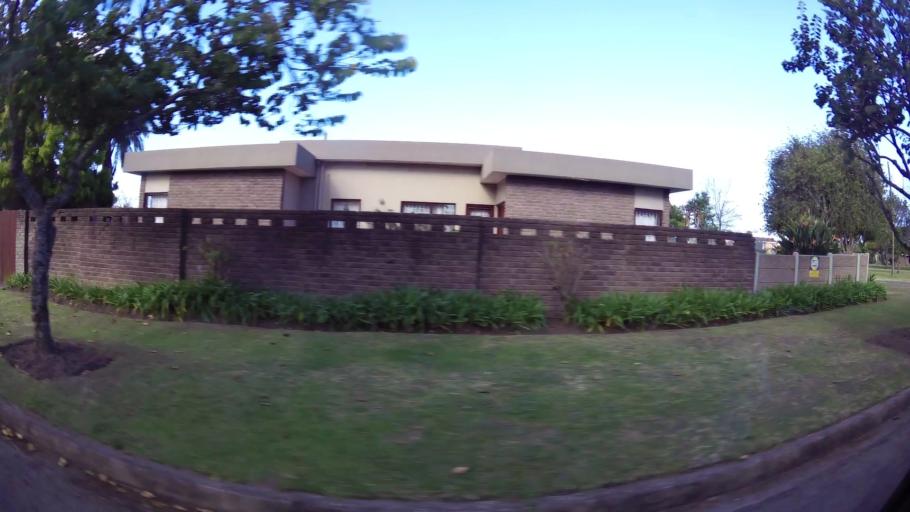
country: ZA
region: Western Cape
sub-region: Eden District Municipality
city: George
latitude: -33.9631
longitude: 22.4878
